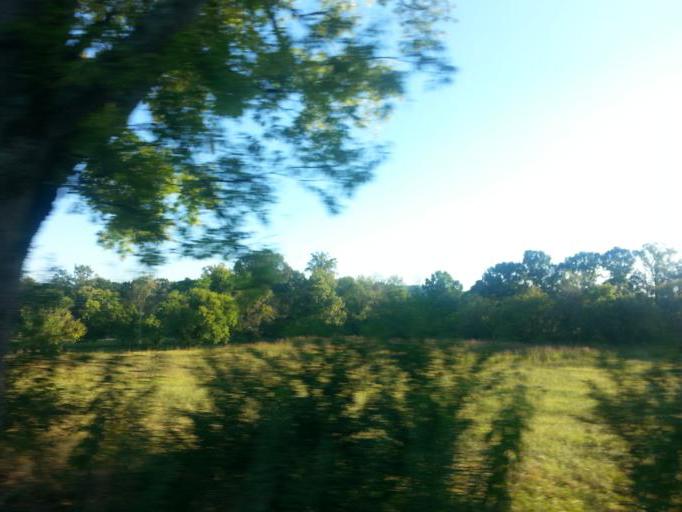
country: US
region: Tennessee
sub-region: Blount County
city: Eagleton Village
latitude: 35.8186
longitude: -83.9116
